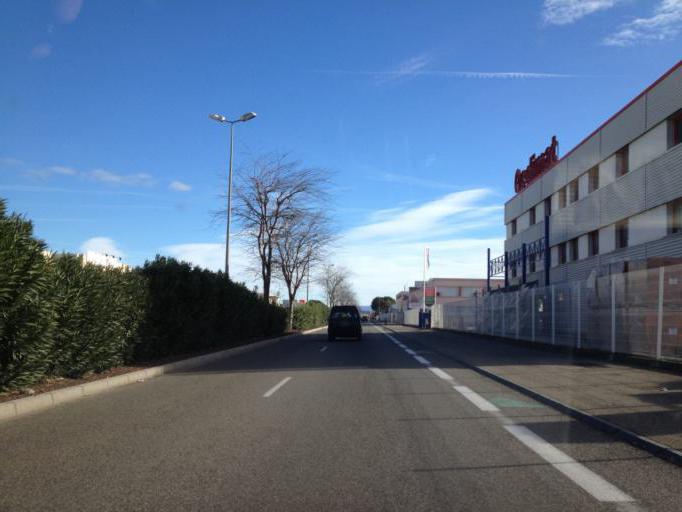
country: FR
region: Provence-Alpes-Cote d'Azur
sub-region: Departement du Vaucluse
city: Le Pontet
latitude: 43.9392
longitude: 4.8388
